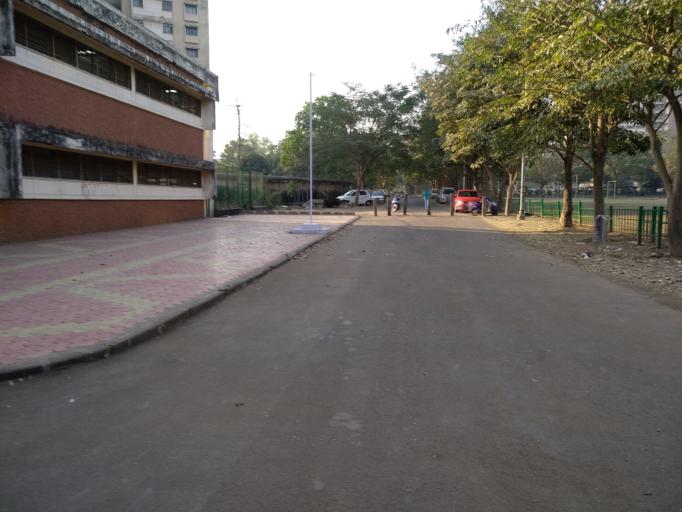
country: IN
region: Maharashtra
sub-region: Mumbai Suburban
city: Mumbai
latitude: 19.0369
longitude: 72.9266
